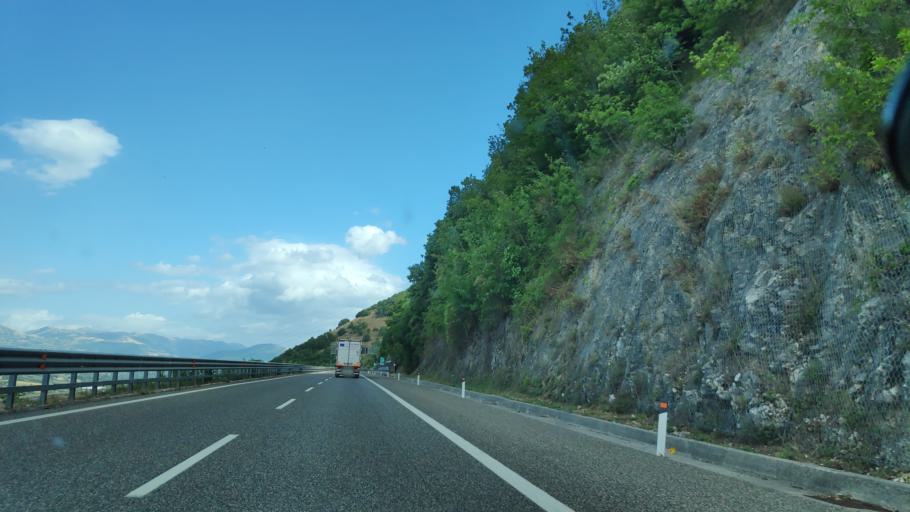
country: IT
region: Campania
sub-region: Provincia di Salerno
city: Sicignano degli Alburni
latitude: 40.5863
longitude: 15.3373
